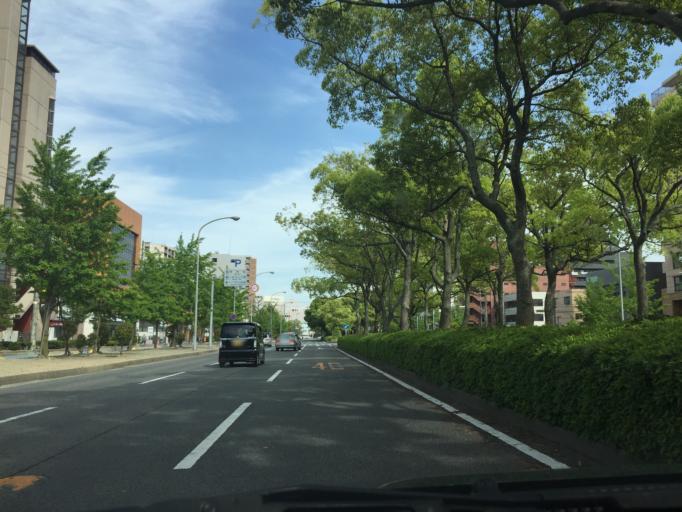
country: JP
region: Mie
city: Yokkaichi
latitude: 34.9689
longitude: 136.6112
